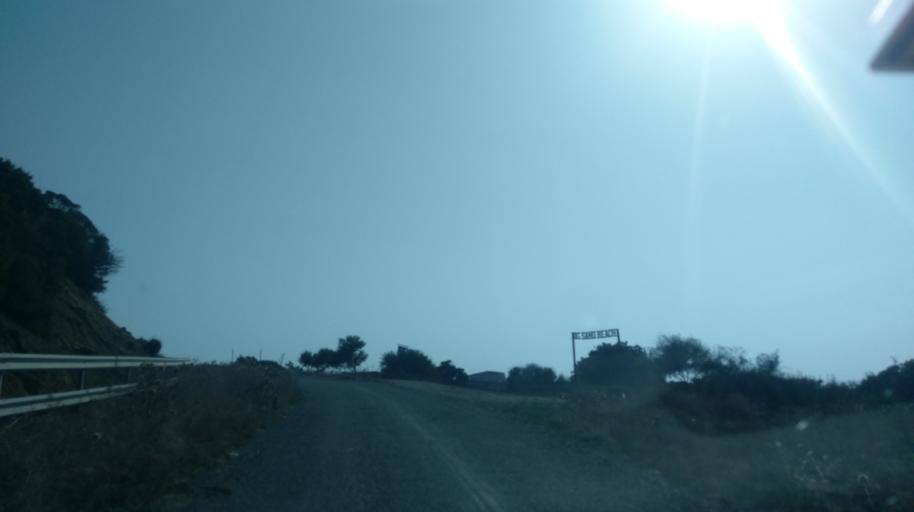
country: CY
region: Ammochostos
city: Rizokarpaso
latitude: 35.6458
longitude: 34.5537
